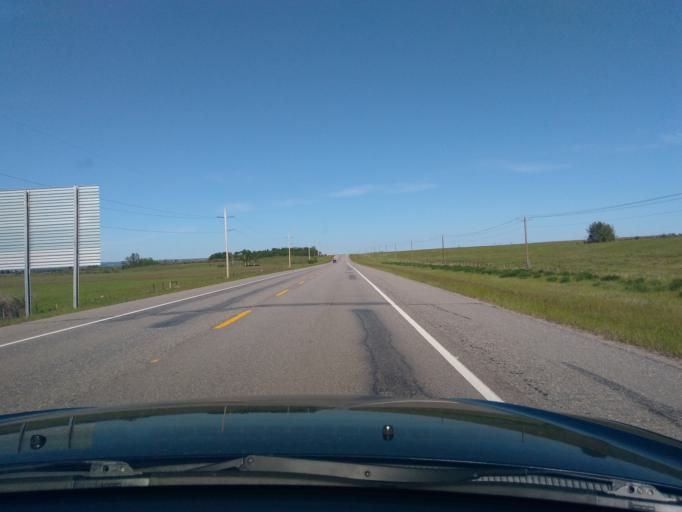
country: CA
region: Alberta
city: Cochrane
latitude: 51.0234
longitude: -114.4538
